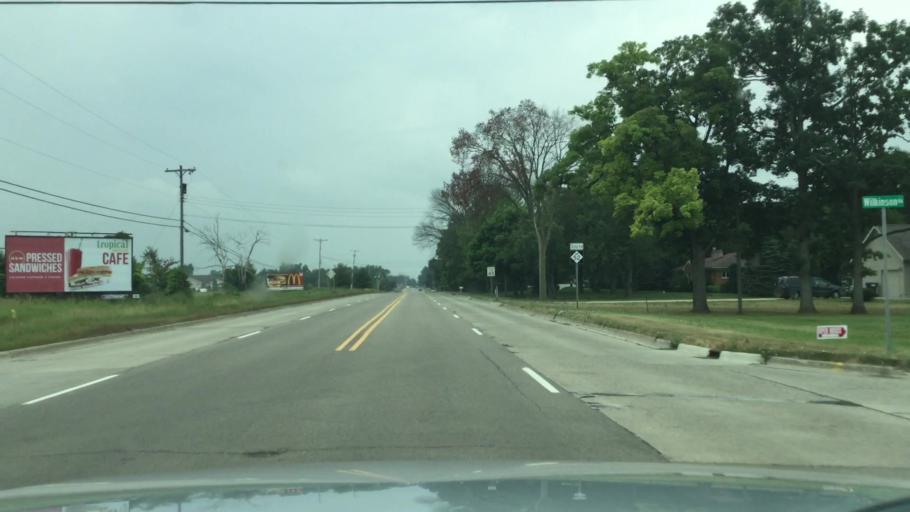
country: US
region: Michigan
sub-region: Shiawassee County
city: Owosso
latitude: 43.0266
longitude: -84.1769
